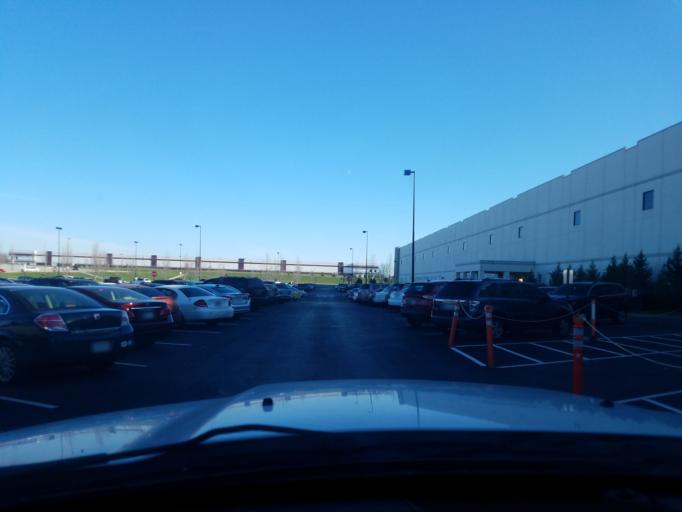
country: US
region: Indiana
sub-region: Clark County
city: Sellersburg
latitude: 38.3795
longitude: -85.6856
